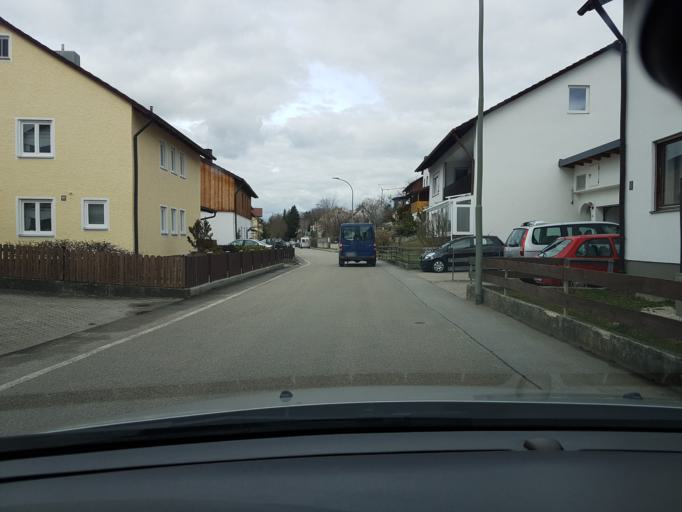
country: DE
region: Bavaria
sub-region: Lower Bavaria
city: Vilsbiburg
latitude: 48.4553
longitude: 12.3493
